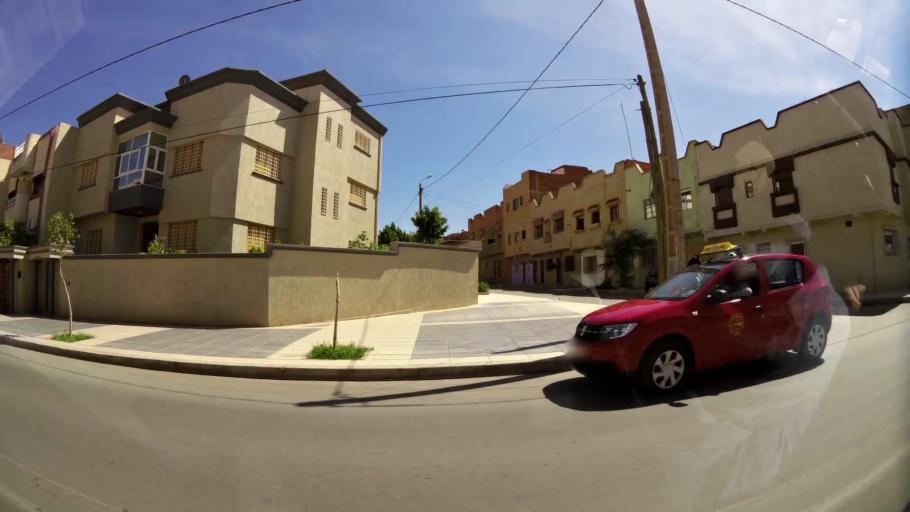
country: MA
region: Oriental
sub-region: Oujda-Angad
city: Oujda
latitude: 34.6564
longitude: -1.9020
